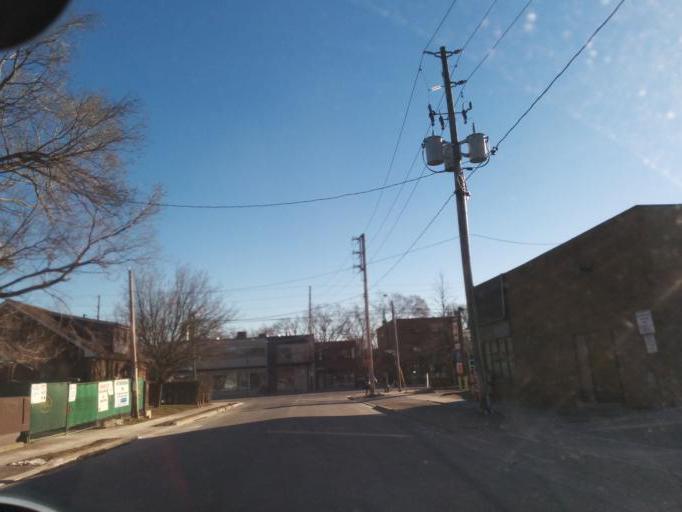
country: CA
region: Ontario
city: Etobicoke
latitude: 43.5976
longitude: -79.5227
